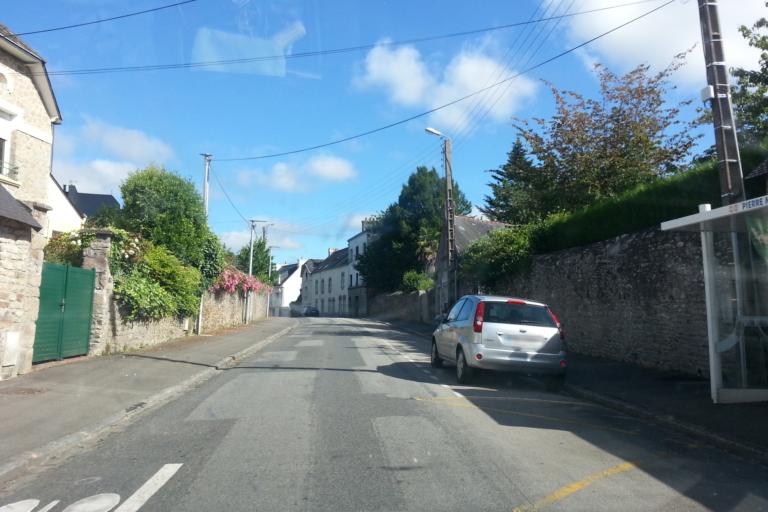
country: FR
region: Brittany
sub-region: Departement du Morbihan
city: Hennebont
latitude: 47.8079
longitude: -3.2720
